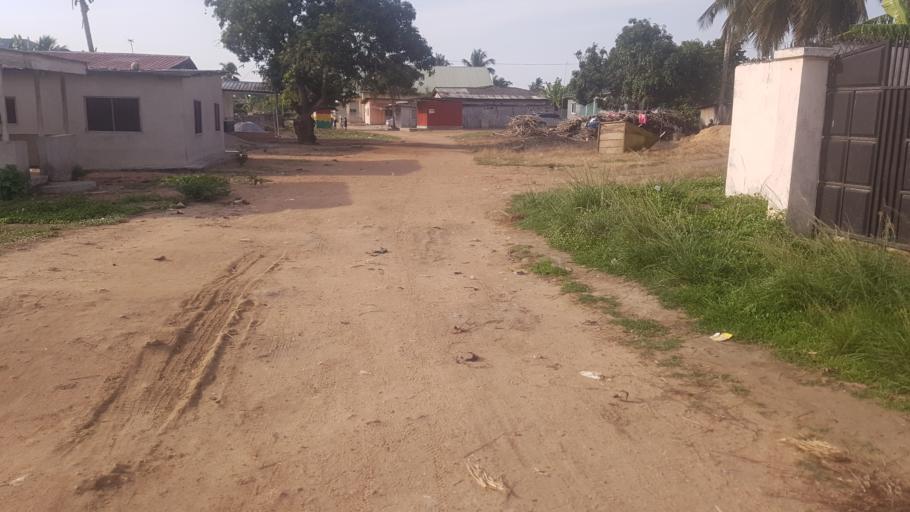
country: GH
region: Central
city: Winneba
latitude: 5.3567
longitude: -0.6305
